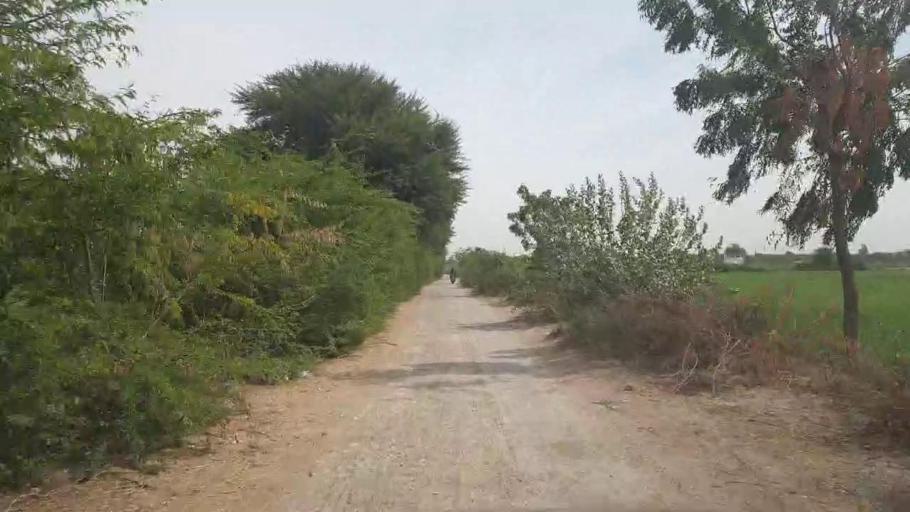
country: PK
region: Sindh
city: Umarkot
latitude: 25.2521
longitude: 69.7064
